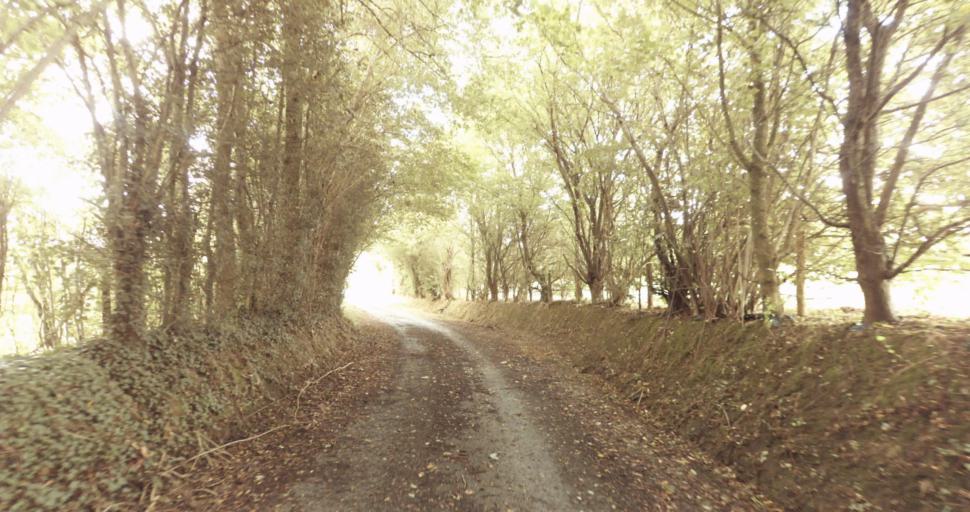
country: FR
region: Lower Normandy
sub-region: Departement de l'Orne
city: Sainte-Gauburge-Sainte-Colombe
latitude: 48.7084
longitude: 0.3924
